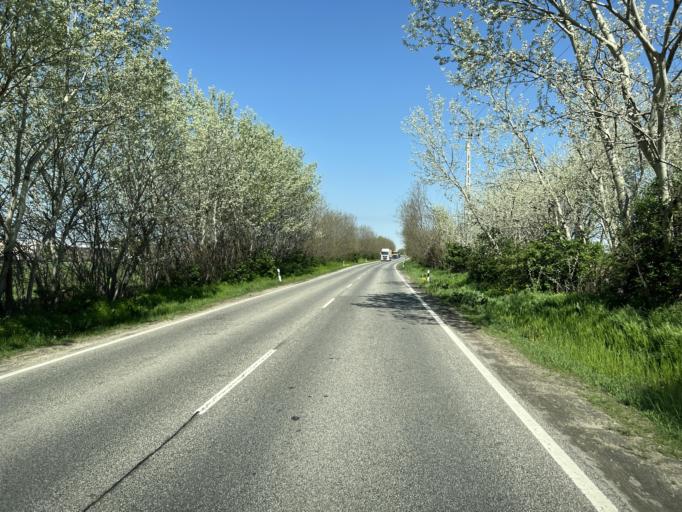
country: HU
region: Pest
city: Alsonemedi
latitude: 47.3470
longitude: 19.1676
